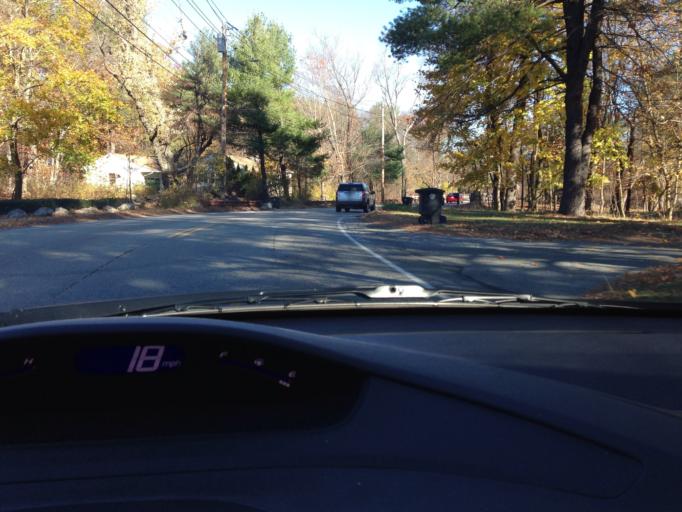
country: US
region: Massachusetts
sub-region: Middlesex County
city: Bedford
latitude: 42.4962
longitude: -71.2580
